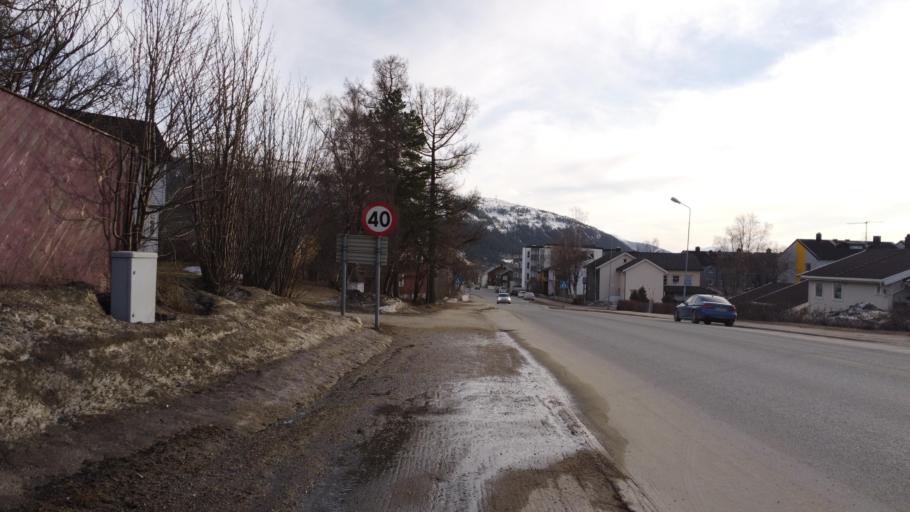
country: NO
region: Nordland
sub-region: Rana
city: Mo i Rana
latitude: 66.3154
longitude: 14.1557
